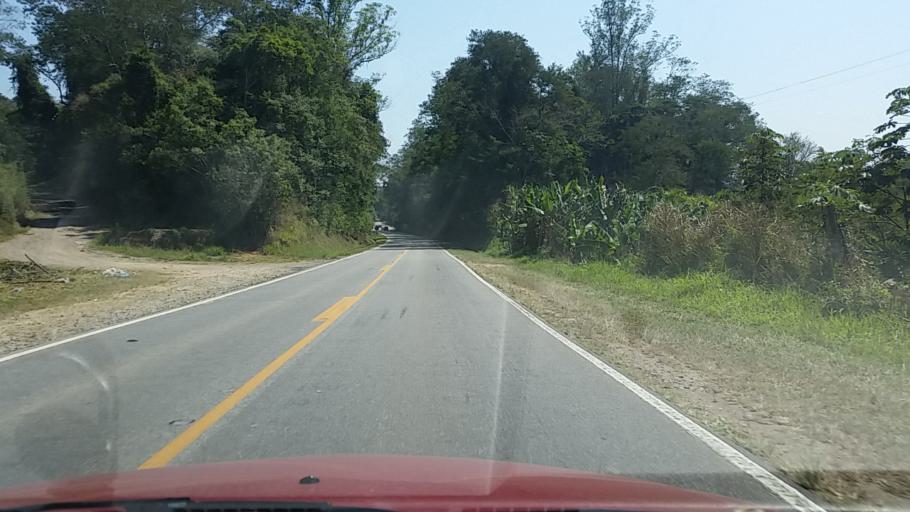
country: BR
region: Sao Paulo
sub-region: Miracatu
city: Miracatu
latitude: -24.3219
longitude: -47.5098
